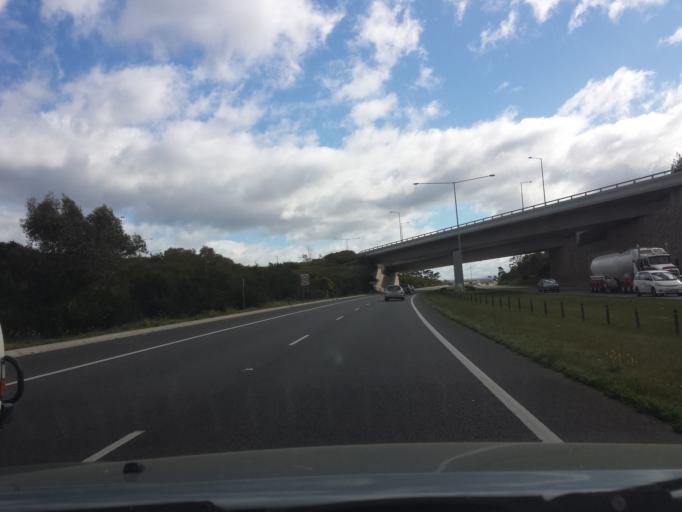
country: AU
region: Victoria
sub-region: Hume
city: Craigieburn
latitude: -37.6019
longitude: 144.9603
